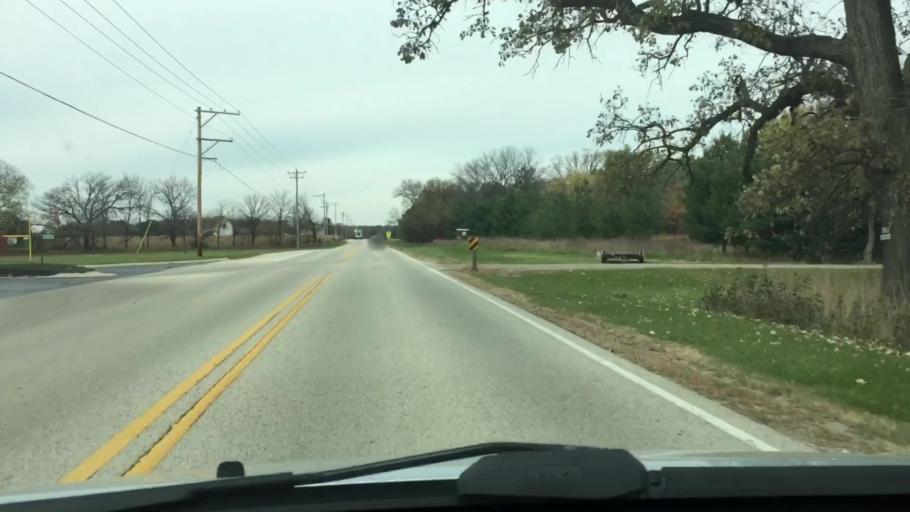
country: US
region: Wisconsin
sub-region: Waukesha County
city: Mukwonago
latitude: 42.8885
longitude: -88.3785
